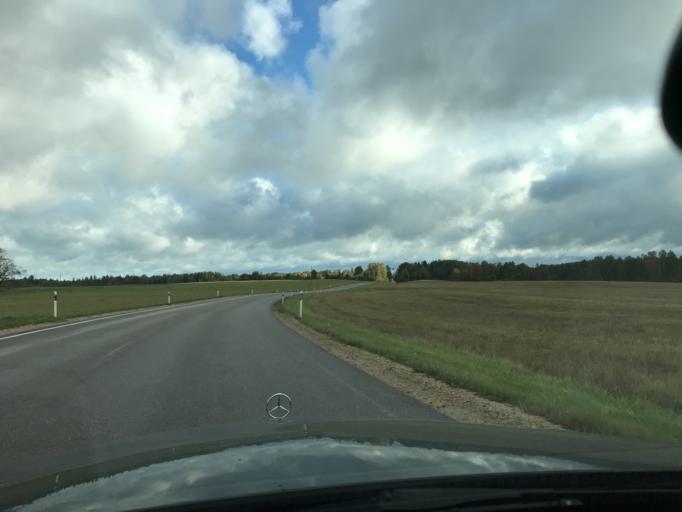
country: EE
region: Valgamaa
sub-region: Torva linn
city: Torva
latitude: 58.0160
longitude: 25.7982
